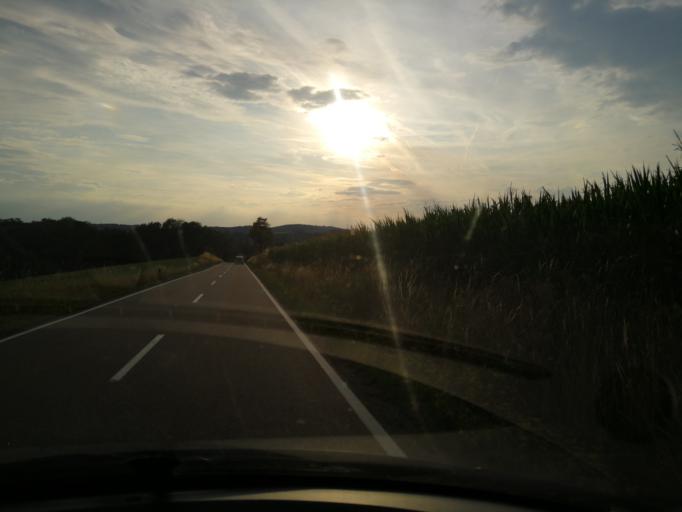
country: DE
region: Bavaria
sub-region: Lower Bavaria
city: Wiesenfelden
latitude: 49.0448
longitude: 12.5537
